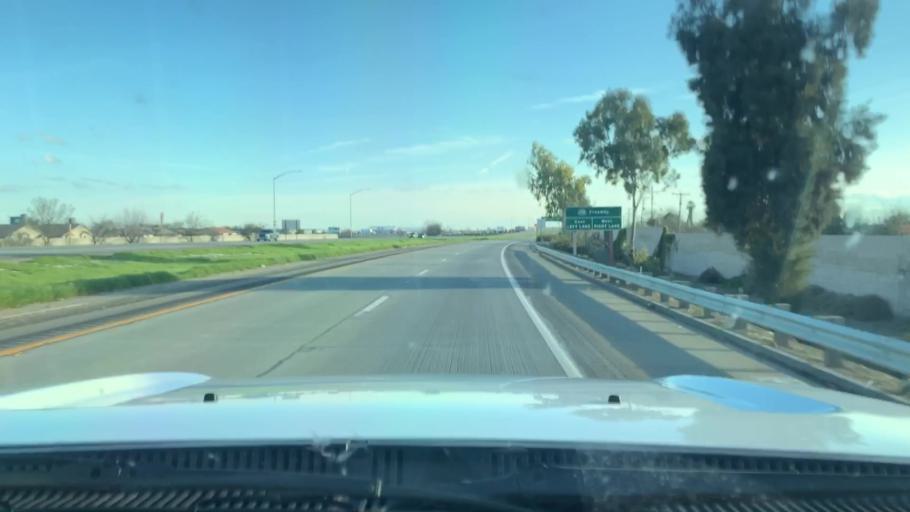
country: US
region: California
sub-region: Kings County
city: Lemoore
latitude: 36.2889
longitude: -119.8083
